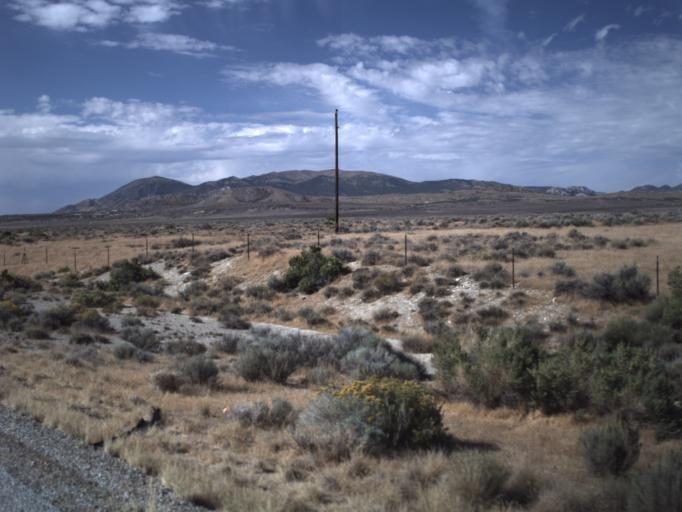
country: US
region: Utah
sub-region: Tooele County
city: Wendover
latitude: 41.5613
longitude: -113.5830
